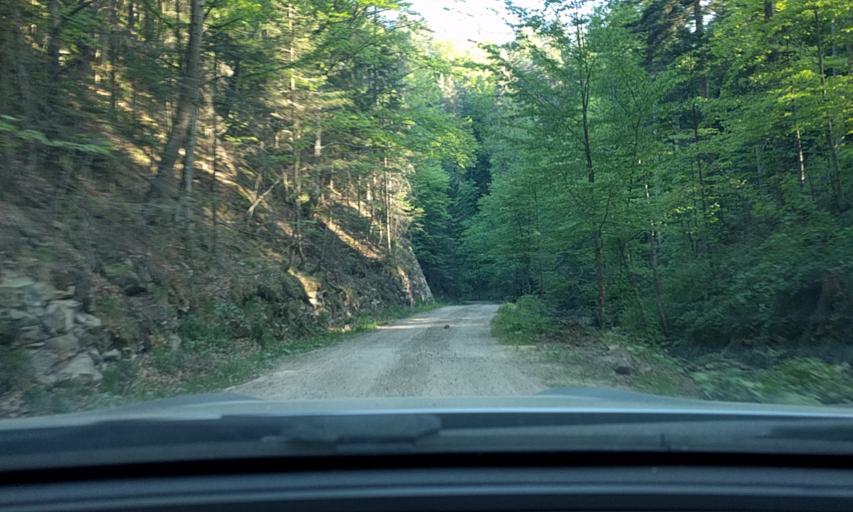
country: RO
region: Bacau
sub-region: Comuna Oituz
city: Ferestrau-Oituz
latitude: 46.1385
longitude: 26.5391
